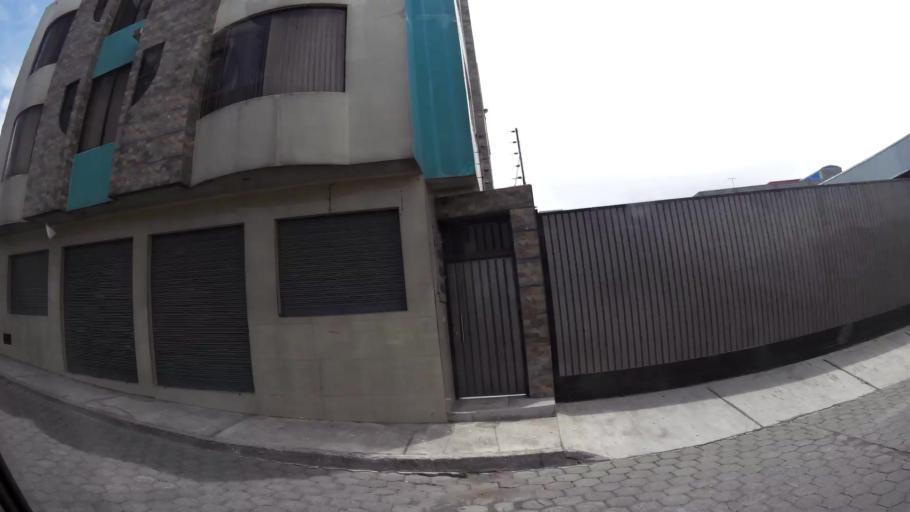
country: EC
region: Cotopaxi
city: San Miguel de Salcedo
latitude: -1.0442
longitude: -78.5837
